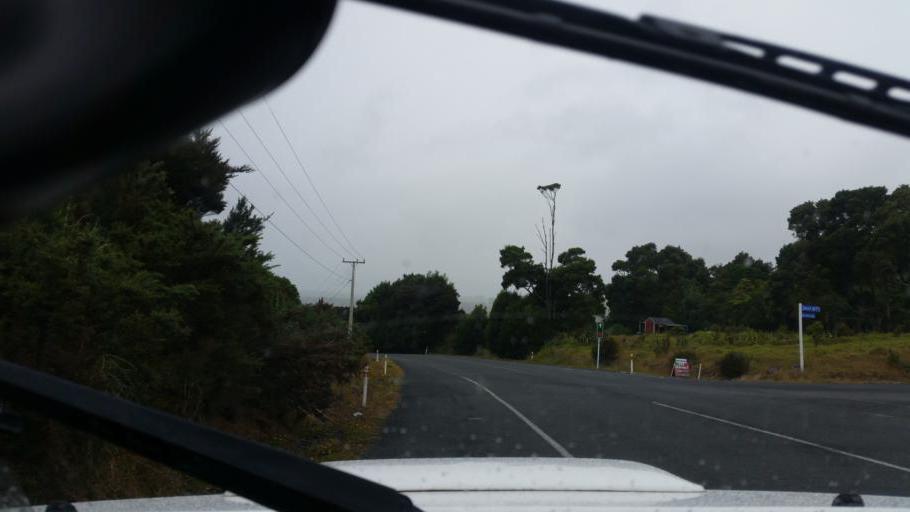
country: NZ
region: Auckland
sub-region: Auckland
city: Wellsford
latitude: -36.1314
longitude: 174.5556
